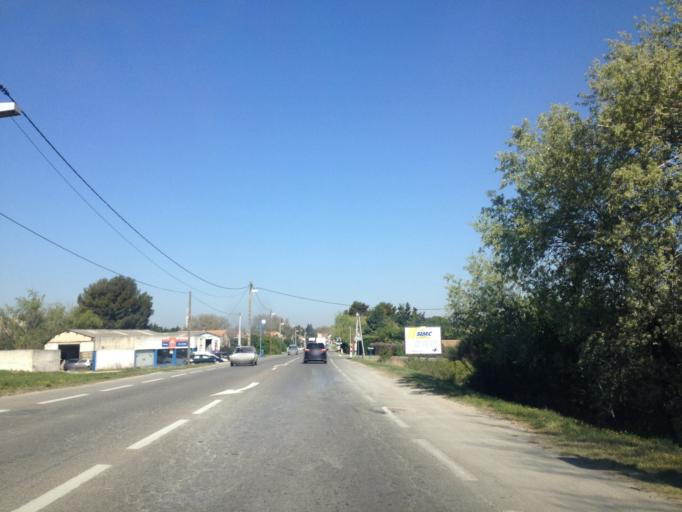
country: FR
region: Provence-Alpes-Cote d'Azur
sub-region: Departement du Vaucluse
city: Sarrians
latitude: 44.0823
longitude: 4.9785
